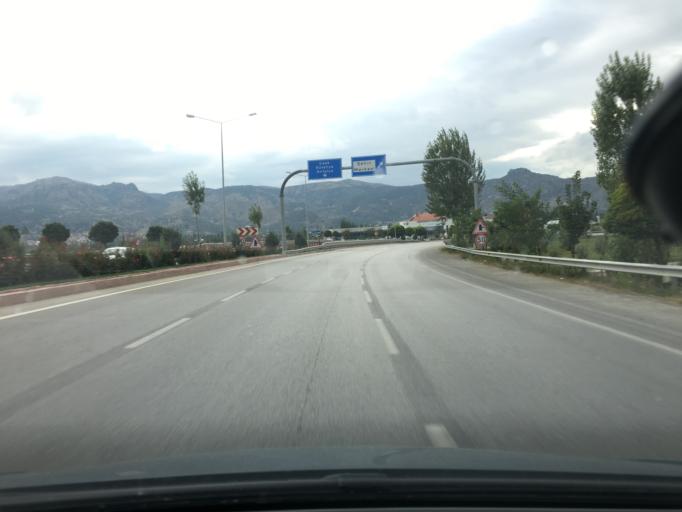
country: TR
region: Afyonkarahisar
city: Afyonkarahisar
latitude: 38.7806
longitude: 30.4955
